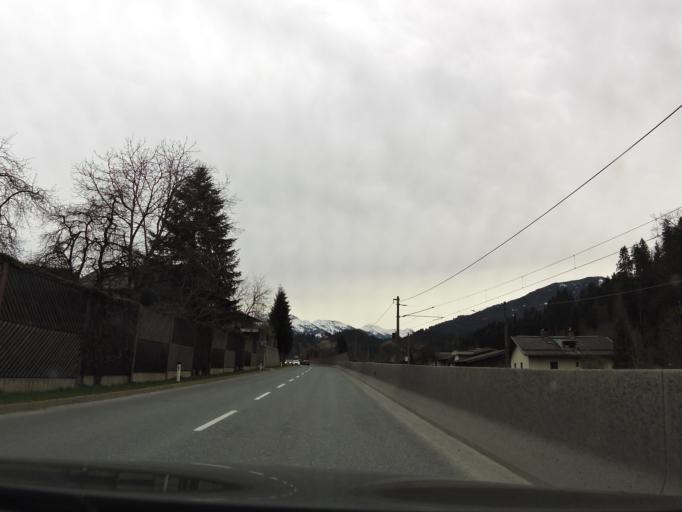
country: AT
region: Tyrol
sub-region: Politischer Bezirk Kitzbuhel
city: Hopfgarten im Brixental
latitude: 47.4492
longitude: 12.1551
